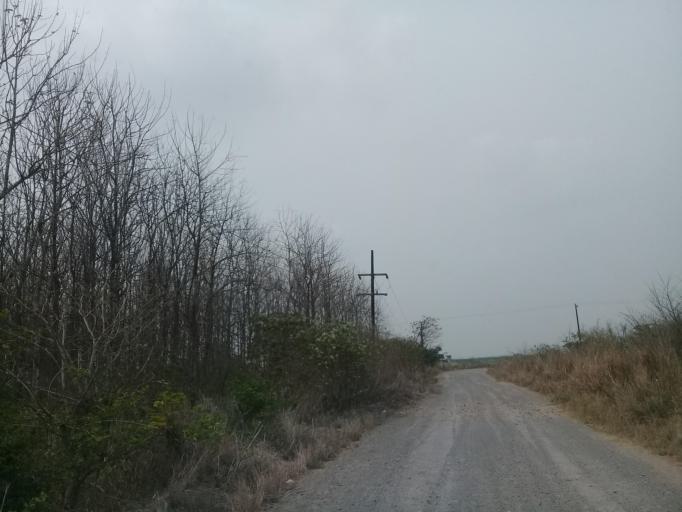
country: MX
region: Veracruz
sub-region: Medellin
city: La Laguna y Monte del Castillo
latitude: 18.9046
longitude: -96.1777
